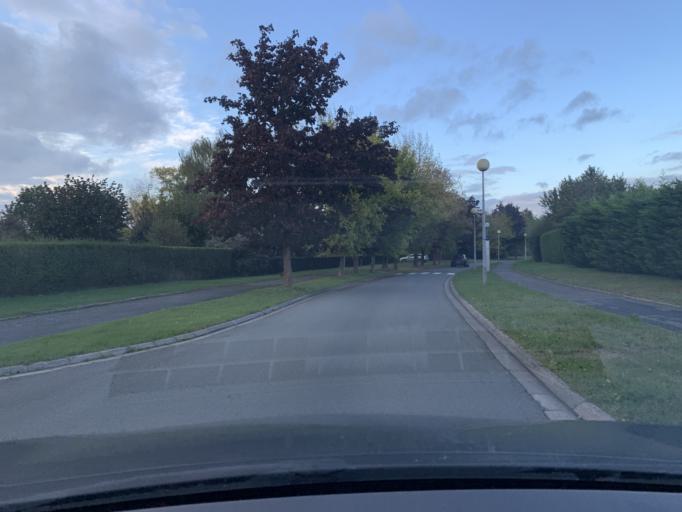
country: FR
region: Nord-Pas-de-Calais
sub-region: Departement du Nord
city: Proville
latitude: 50.1571
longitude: 3.2107
